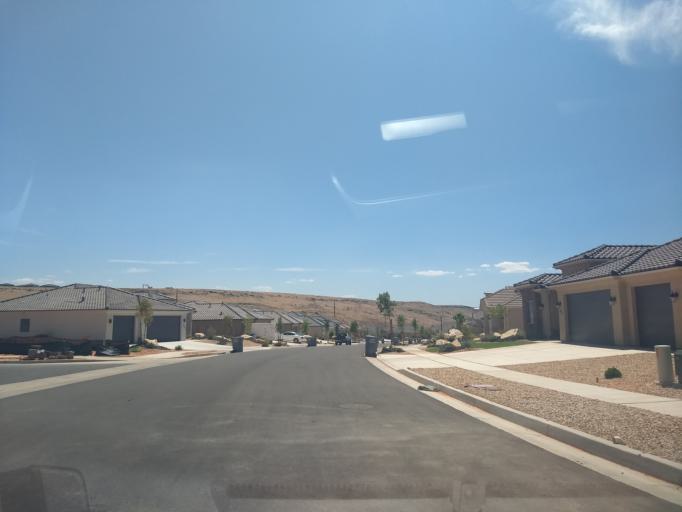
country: US
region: Utah
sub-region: Washington County
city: Washington
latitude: 37.1406
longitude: -113.4789
